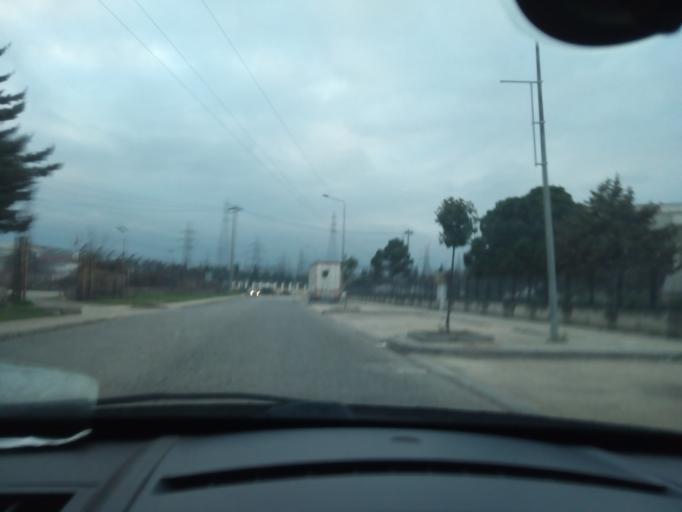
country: TR
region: Bursa
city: Niluefer
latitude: 40.2363
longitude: 28.9679
